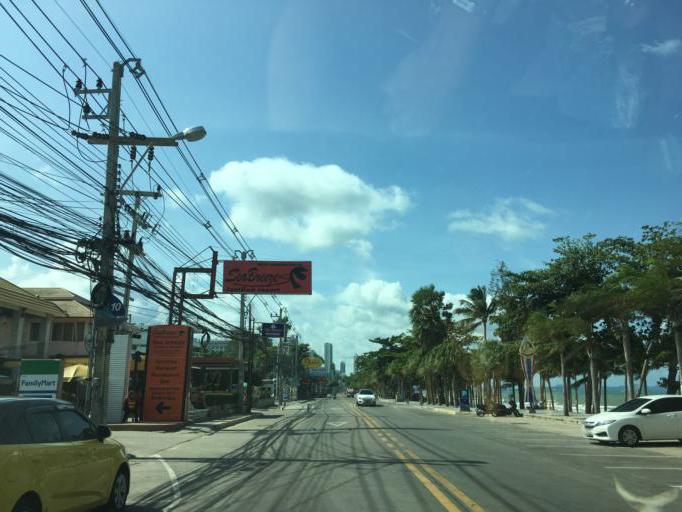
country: TH
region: Chon Buri
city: Phatthaya
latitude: 12.8895
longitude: 100.8753
